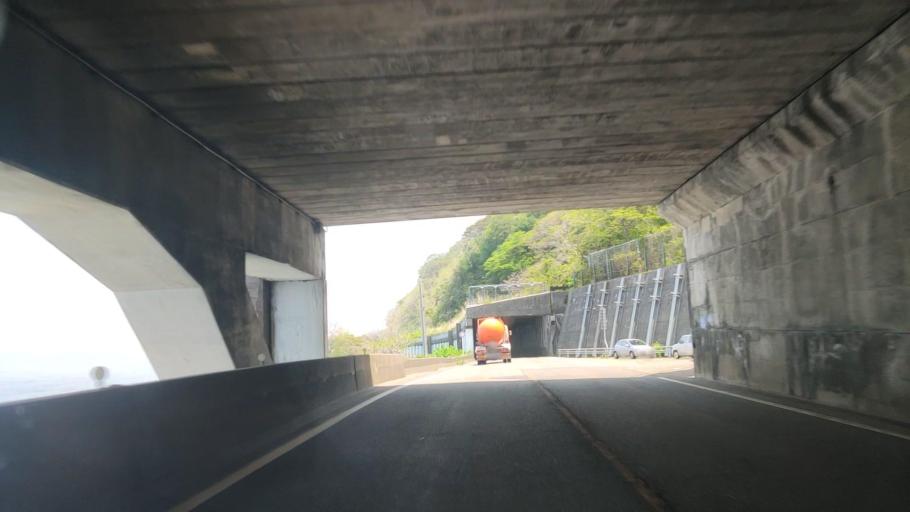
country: JP
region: Niigata
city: Itoigawa
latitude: 37.0186
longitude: 137.7726
